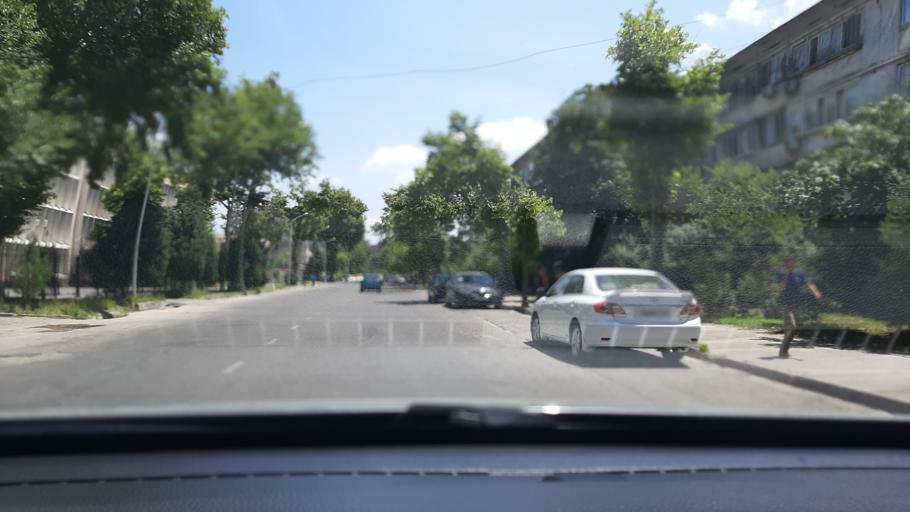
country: TJ
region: Dushanbe
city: Dushanbe
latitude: 38.5330
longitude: 68.7638
